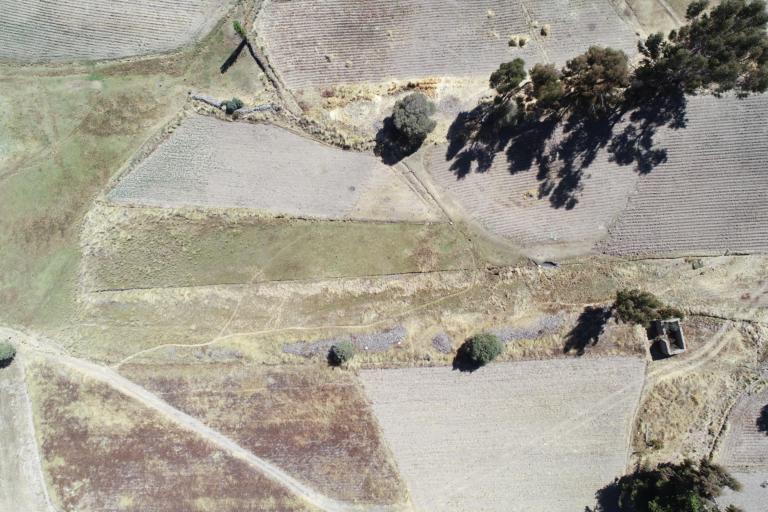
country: BO
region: La Paz
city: Achacachi
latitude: -16.0237
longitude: -68.6170
